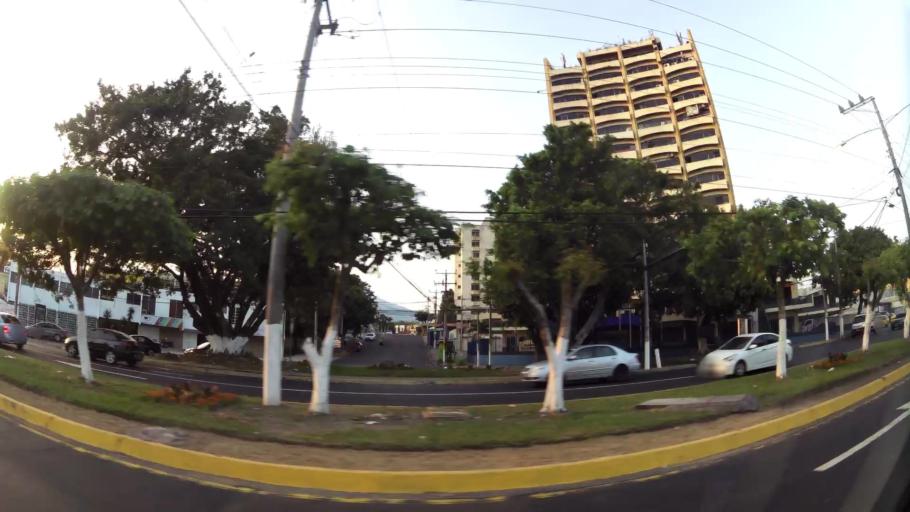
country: SV
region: San Salvador
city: San Salvador
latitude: 13.7111
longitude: -89.2073
